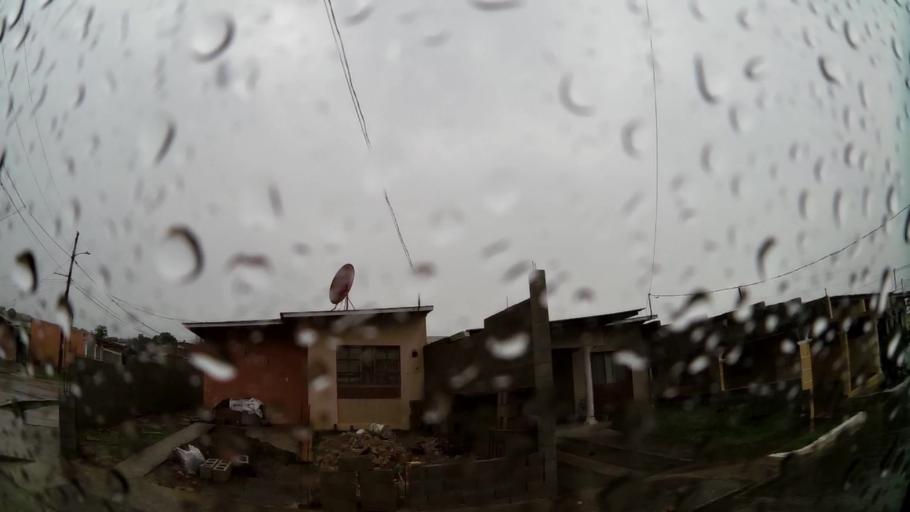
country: PA
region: Colon
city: Puerto Pilon
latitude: 9.3582
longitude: -79.7898
